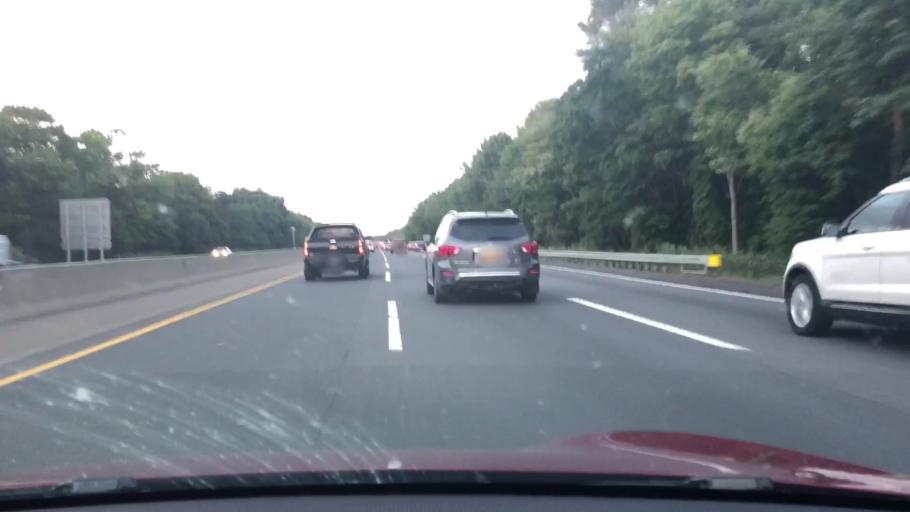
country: US
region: New Jersey
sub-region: Burlington County
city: Ramblewood
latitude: 39.9514
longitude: -74.9266
